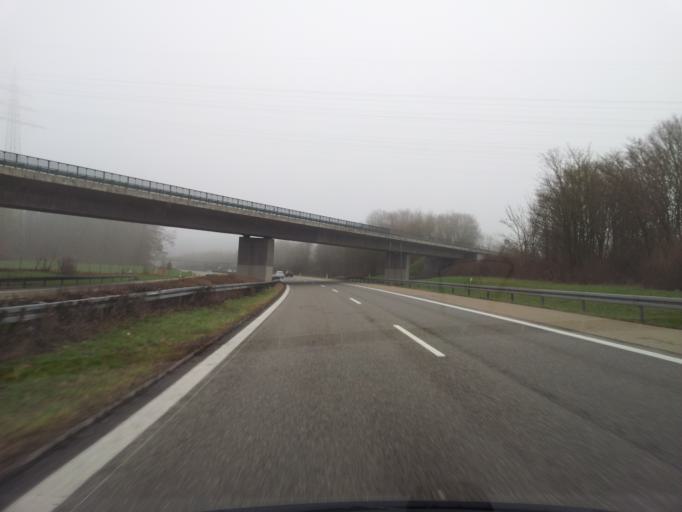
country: DE
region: Baden-Wuerttemberg
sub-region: Freiburg Region
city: Volkertshausen
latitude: 47.8047
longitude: 8.8538
